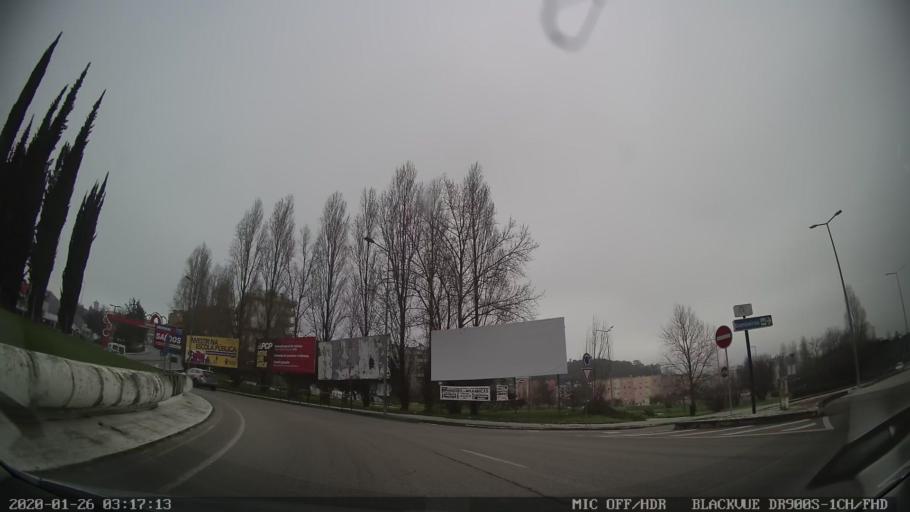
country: PT
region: Santarem
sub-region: Santarem
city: Santarem
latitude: 39.2446
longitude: -8.6905
